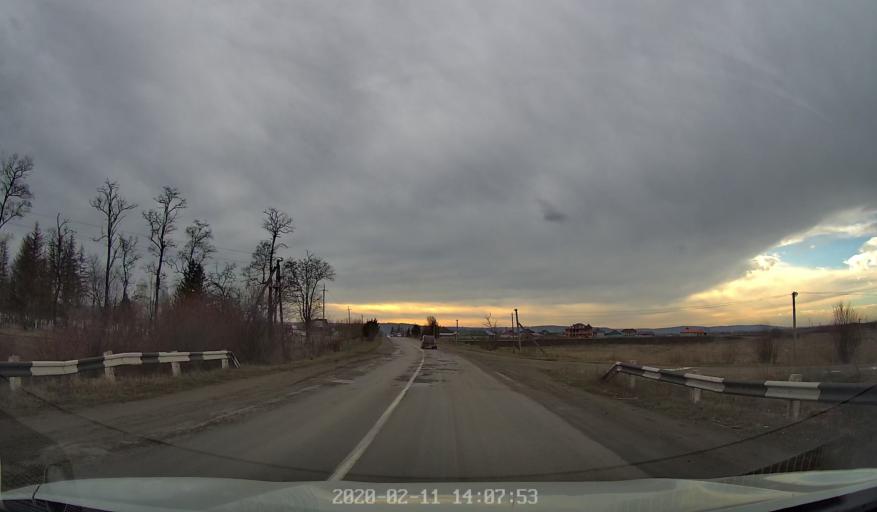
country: RO
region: Botosani
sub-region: Comuna Darabani
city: Bajura
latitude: 48.2429
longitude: 26.5488
